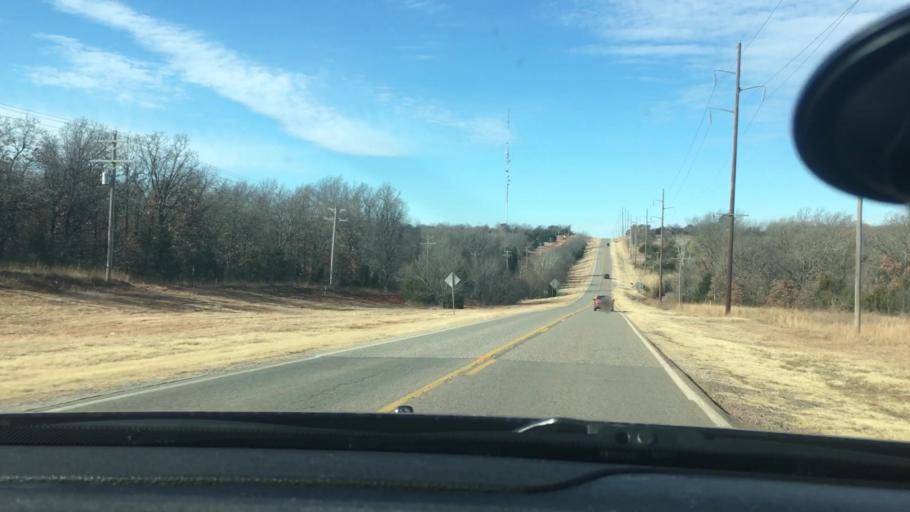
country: US
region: Oklahoma
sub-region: Cleveland County
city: Lexington
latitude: 35.0150
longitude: -97.1775
